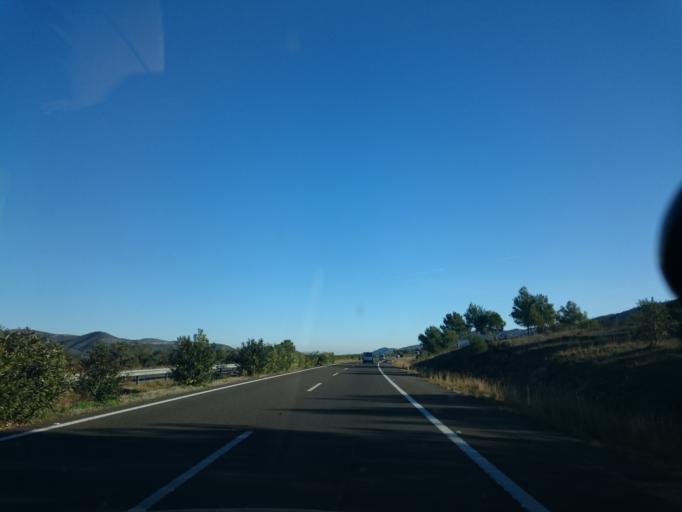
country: ES
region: Valencia
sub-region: Provincia de Castello
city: Santa Magdalena de Pulpis
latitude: 40.3423
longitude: 0.2741
